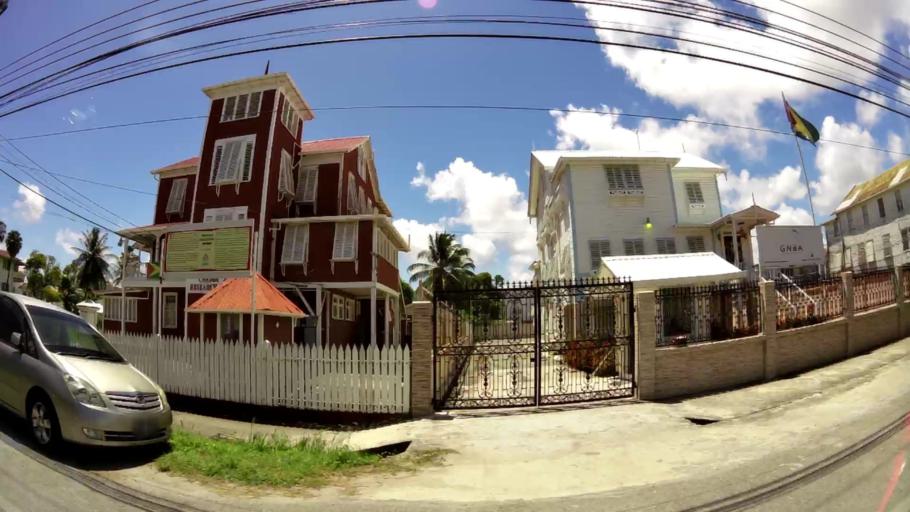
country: GY
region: Demerara-Mahaica
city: Georgetown
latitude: 6.8227
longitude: -58.1626
